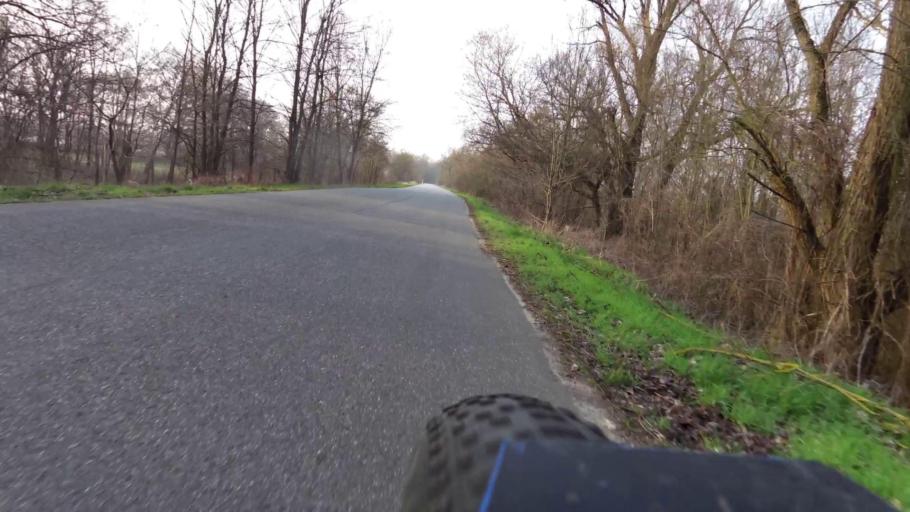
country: DE
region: Brandenburg
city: Vogelsang
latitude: 52.2475
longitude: 14.7066
